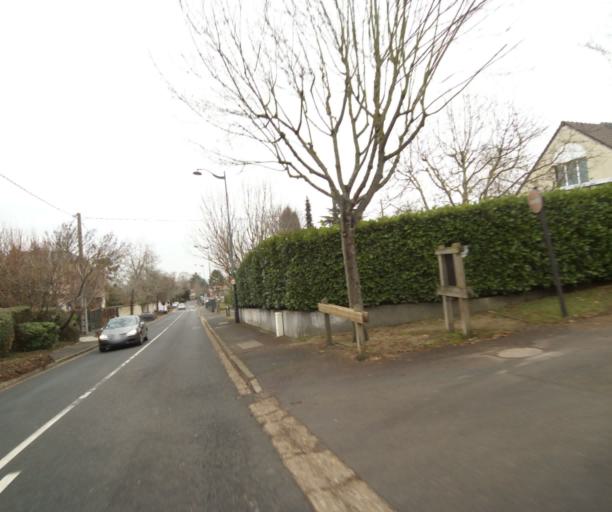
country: FR
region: Ile-de-France
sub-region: Departement des Hauts-de-Seine
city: Rueil-Malmaison
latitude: 48.8656
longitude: 2.1672
